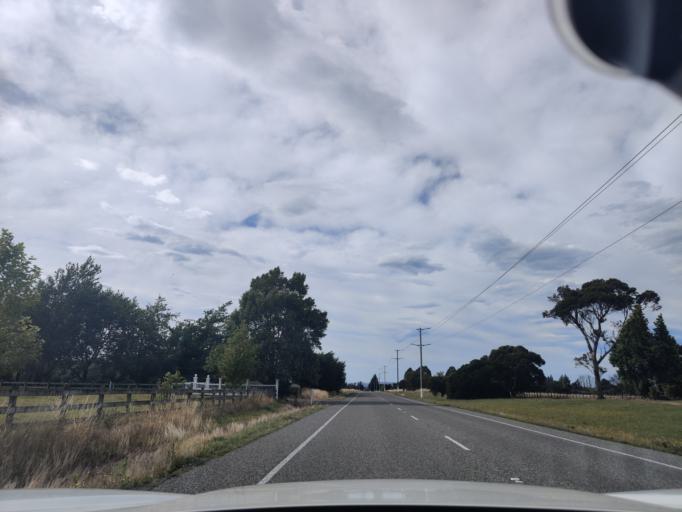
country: NZ
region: Wellington
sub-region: Masterton District
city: Masterton
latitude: -40.8472
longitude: 175.6341
